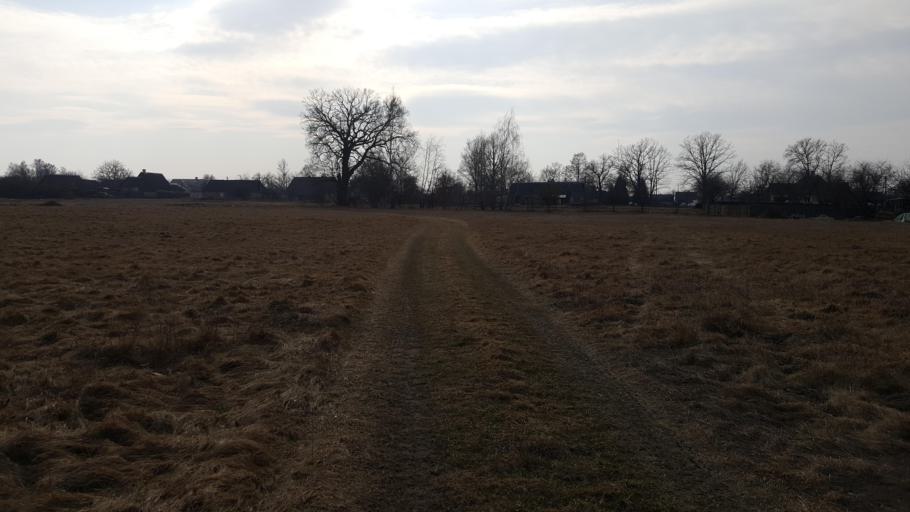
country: BY
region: Brest
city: Kamyanyets
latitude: 52.3147
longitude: 23.9236
